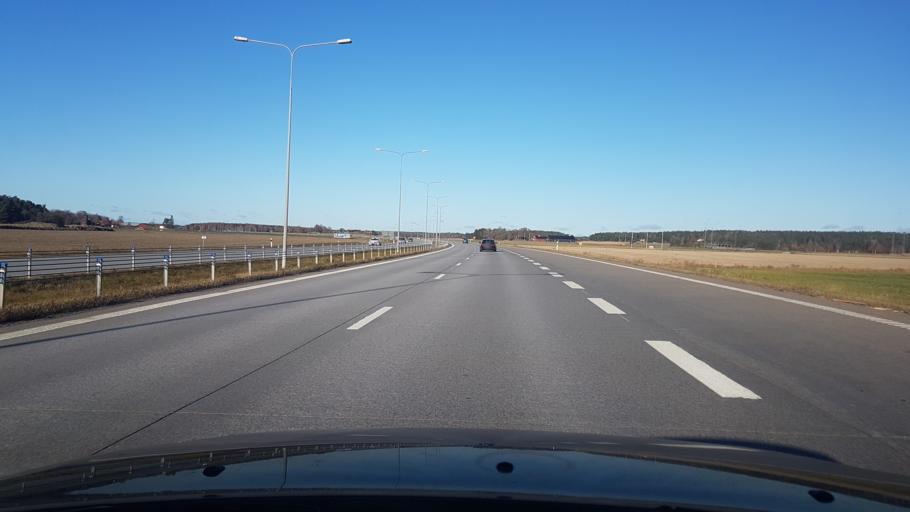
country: SE
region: Uppsala
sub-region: Uppsala Kommun
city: Saevja
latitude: 59.8496
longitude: 17.7343
